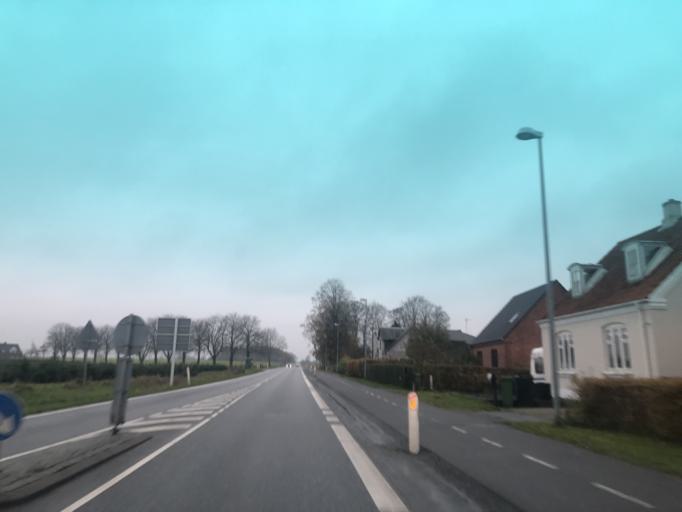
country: DK
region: South Denmark
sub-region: Nyborg Kommune
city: Ullerslev
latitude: 55.2808
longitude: 10.6883
